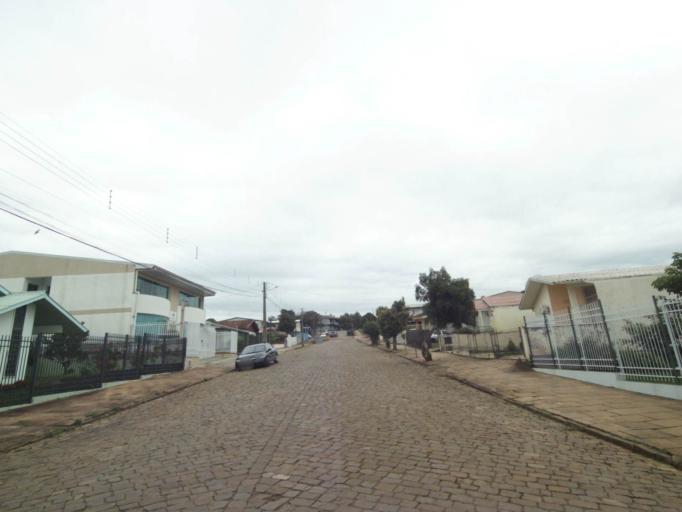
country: BR
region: Rio Grande do Sul
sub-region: Lagoa Vermelha
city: Lagoa Vermelha
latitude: -28.2164
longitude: -51.5249
